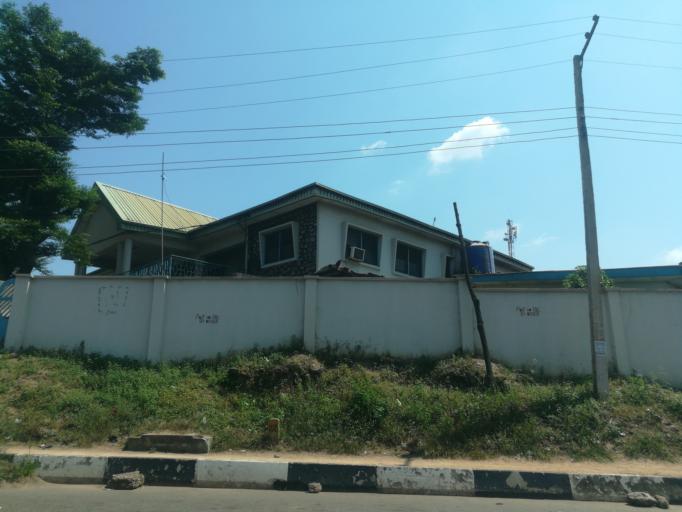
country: NG
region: Ogun
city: Abeokuta
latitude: 7.1635
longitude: 3.3510
